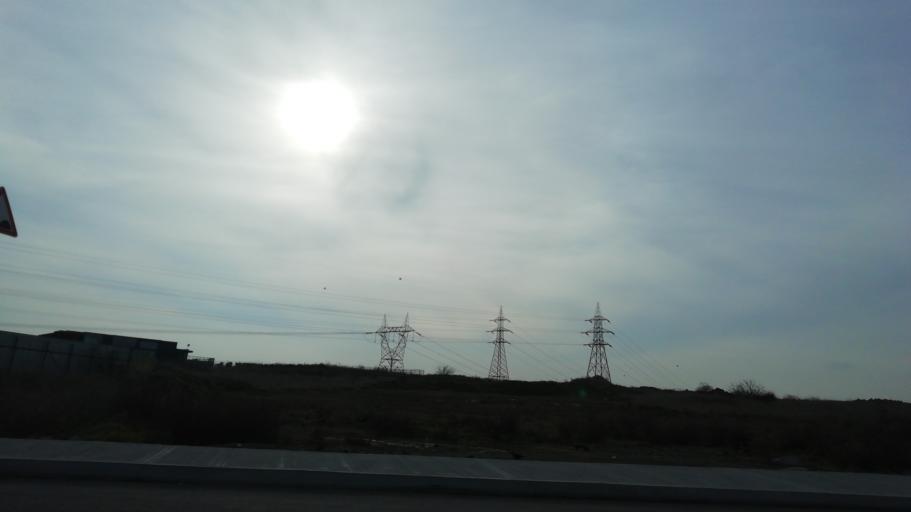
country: TR
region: Istanbul
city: Basaksehir
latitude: 41.1188
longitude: 28.7985
